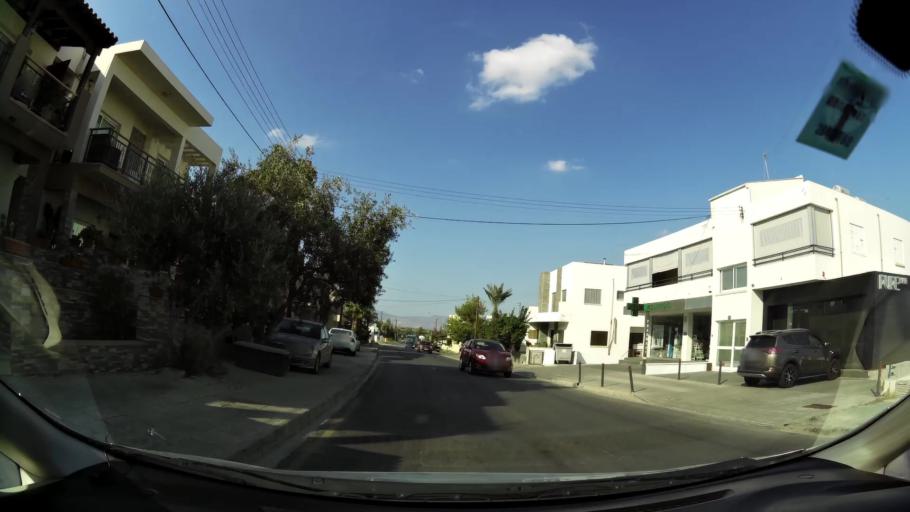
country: CY
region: Lefkosia
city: Kato Deftera
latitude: 35.1232
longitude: 33.2952
